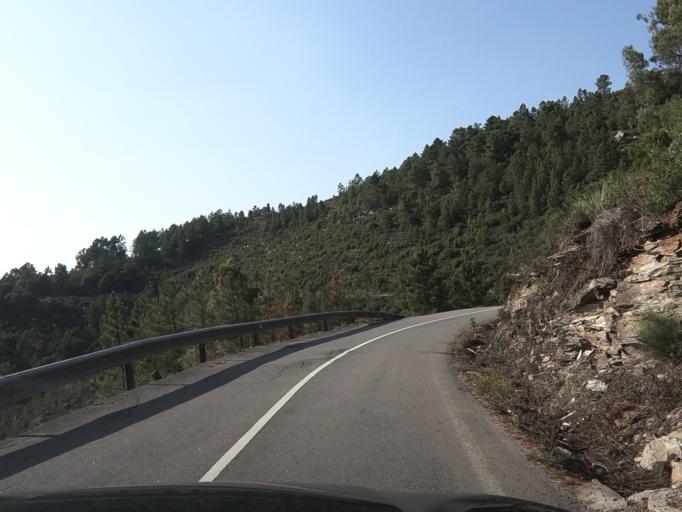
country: PT
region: Vila Real
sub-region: Sabrosa
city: Vilela
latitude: 41.2155
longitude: -7.6193
